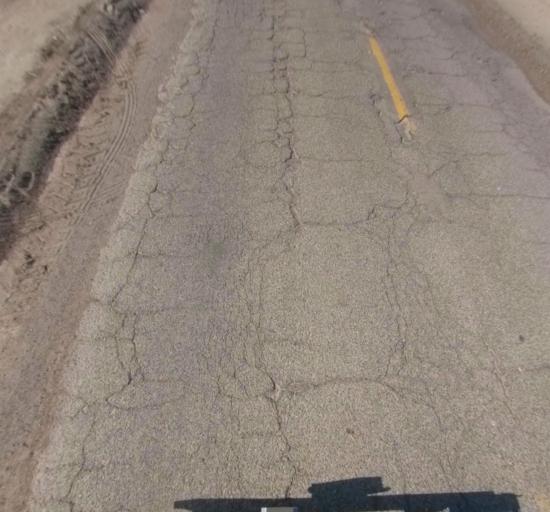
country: US
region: California
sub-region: Madera County
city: Parkwood
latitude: 36.8532
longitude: -120.1283
